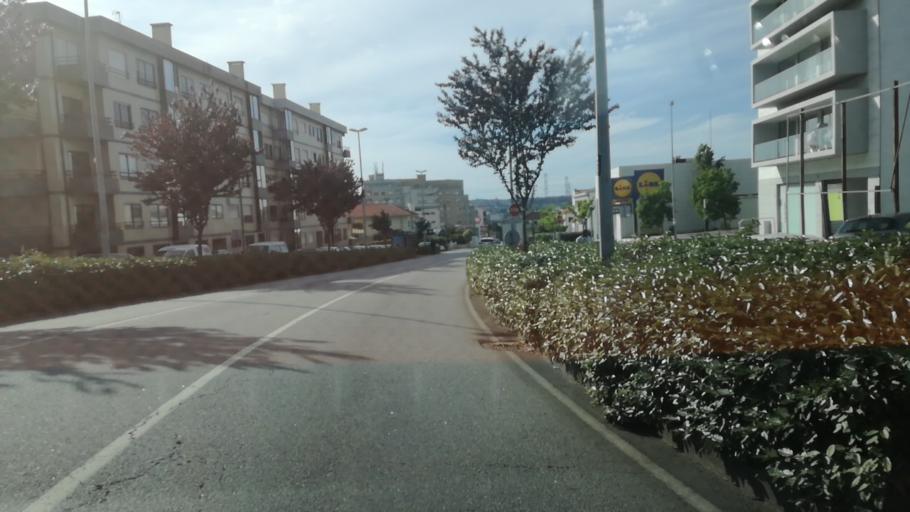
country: PT
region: Porto
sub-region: Maia
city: Milheiros
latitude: 41.2281
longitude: -8.5853
